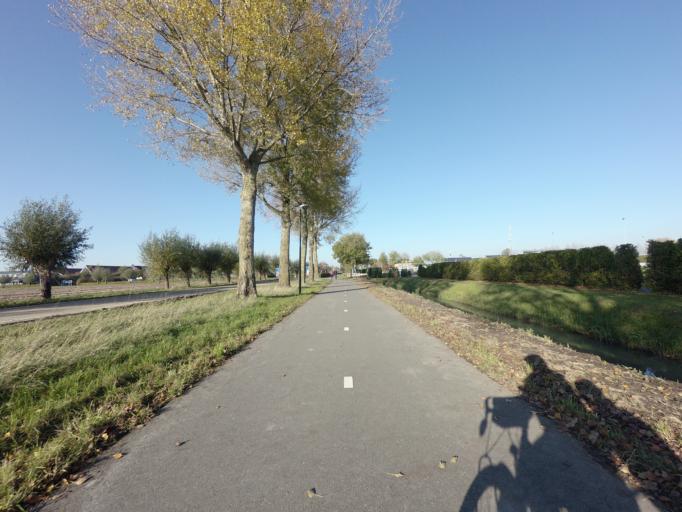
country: NL
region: North Brabant
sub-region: Gemeente Waalwijk
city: Waalwijk
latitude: 51.7274
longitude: 5.0555
